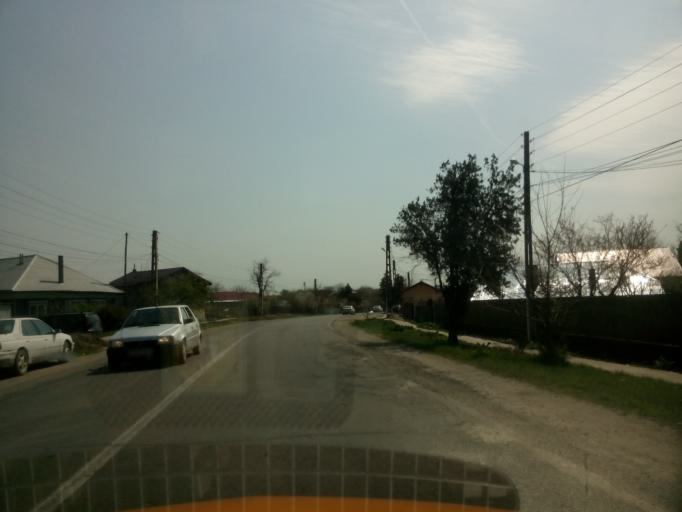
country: RO
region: Calarasi
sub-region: Comuna Soldanu
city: Negoesti
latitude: 44.2294
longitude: 26.5054
